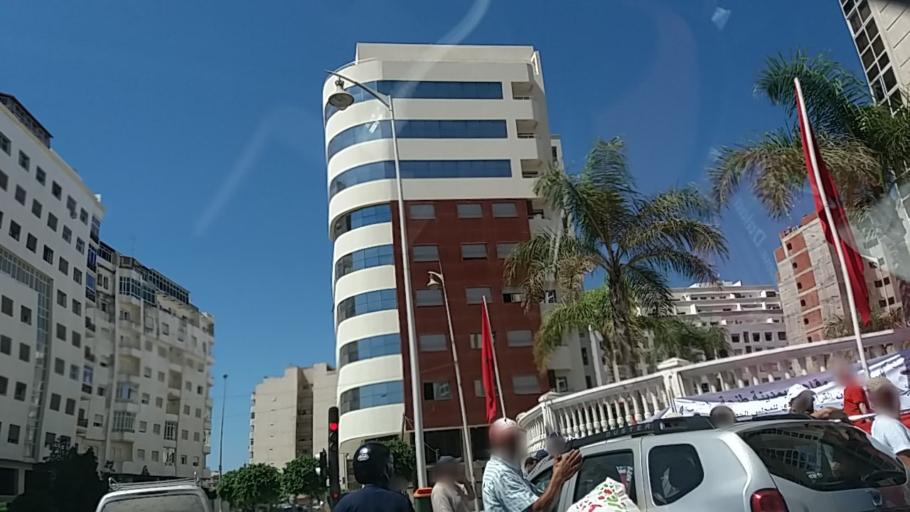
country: MA
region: Tanger-Tetouan
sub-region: Tanger-Assilah
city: Tangier
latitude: 35.7669
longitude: -5.8052
